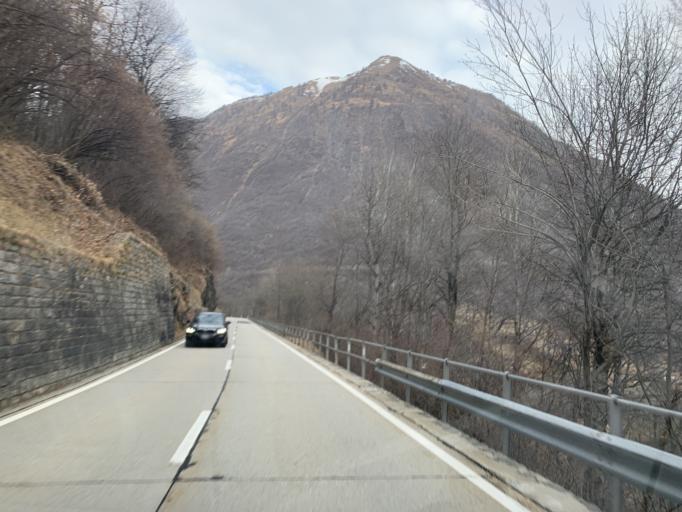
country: CH
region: Ticino
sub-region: Blenio District
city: Acquarossa
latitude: 46.5222
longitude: 8.9325
